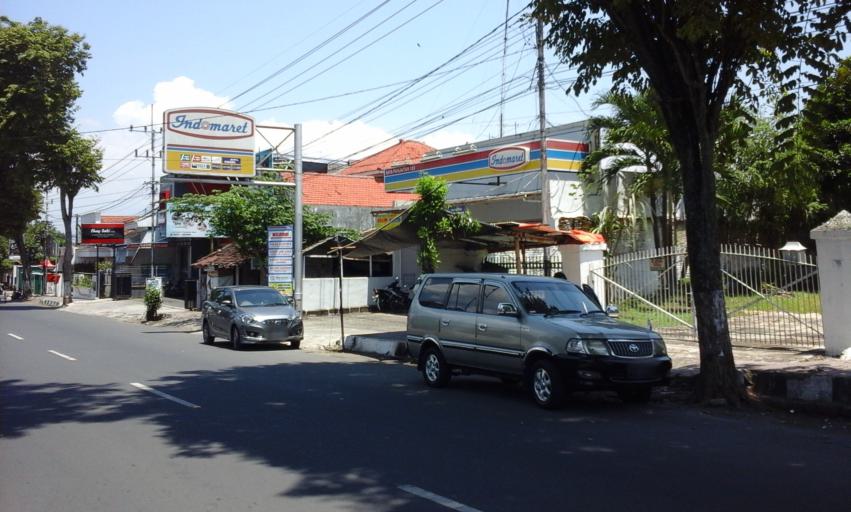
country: ID
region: East Java
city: Sumbersari Wetan
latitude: -8.1809
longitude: 113.7126
